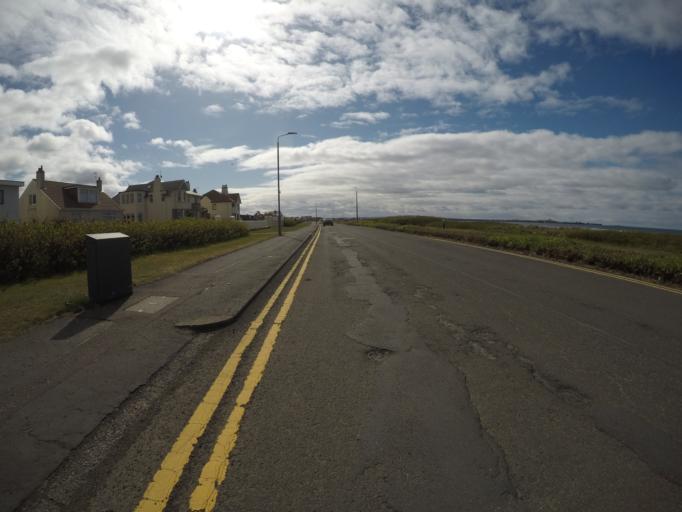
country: GB
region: Scotland
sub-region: South Ayrshire
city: Troon
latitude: 55.5654
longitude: -4.6582
